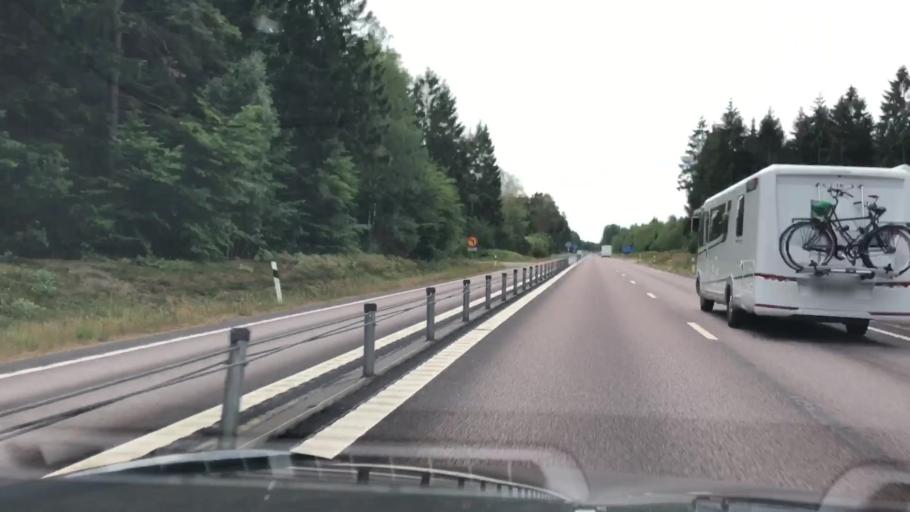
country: SE
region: Blekinge
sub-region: Karlskrona Kommun
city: Jaemjoe
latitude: 56.2530
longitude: 15.9420
